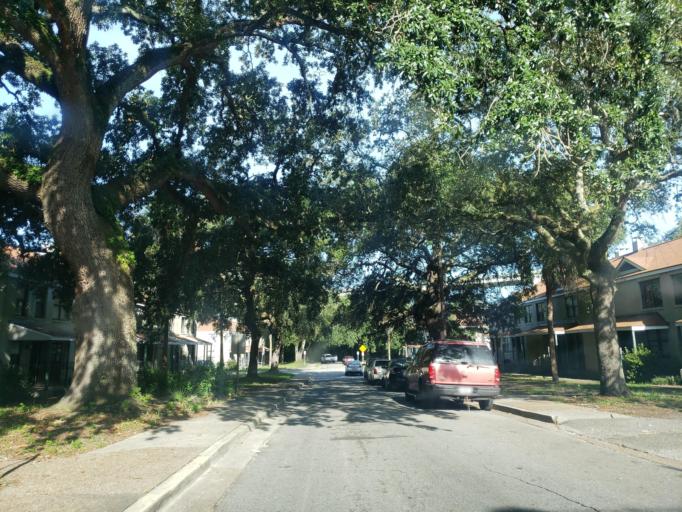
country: US
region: Georgia
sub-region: Chatham County
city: Savannah
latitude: 32.0827
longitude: -81.1007
